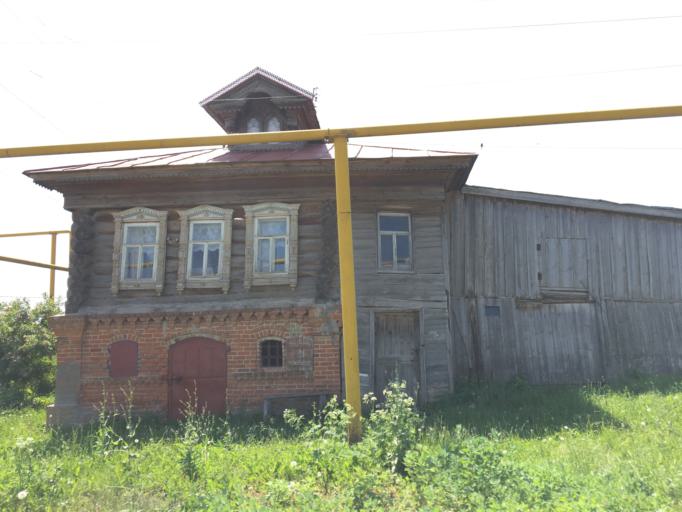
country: RU
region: Nizjnij Novgorod
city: Spasskoye
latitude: 56.1070
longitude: 45.5038
